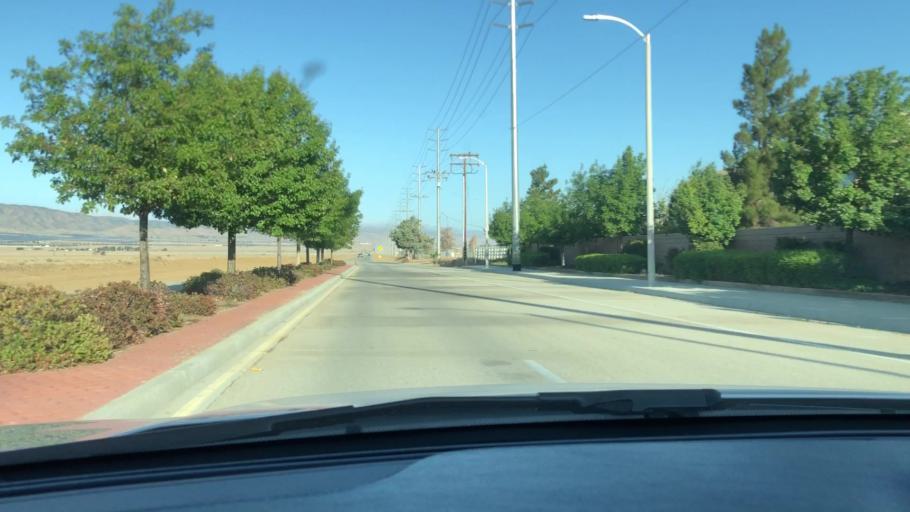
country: US
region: California
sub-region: Los Angeles County
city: Quartz Hill
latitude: 34.6748
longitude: -118.2417
